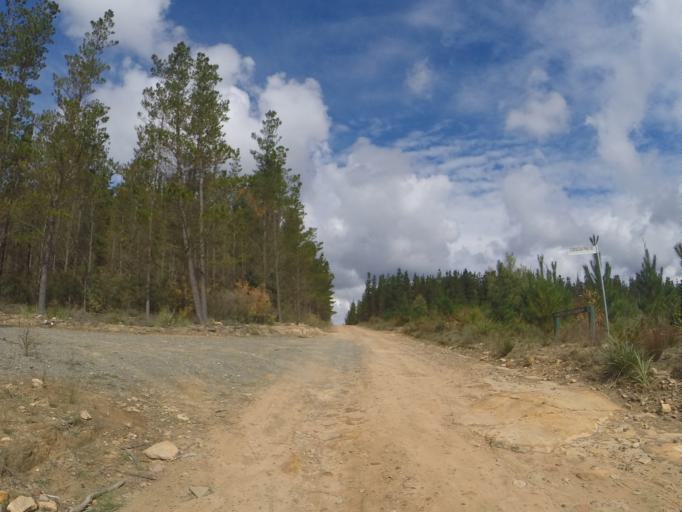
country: AU
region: New South Wales
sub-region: Wingecarribee
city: Moss Vale
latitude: -34.5132
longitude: 150.2307
